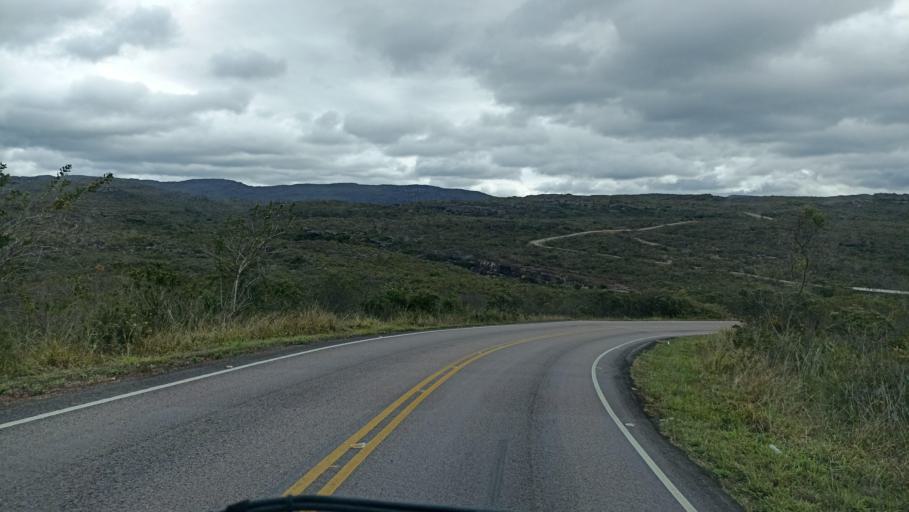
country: BR
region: Bahia
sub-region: Andarai
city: Vera Cruz
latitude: -12.9919
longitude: -41.3455
